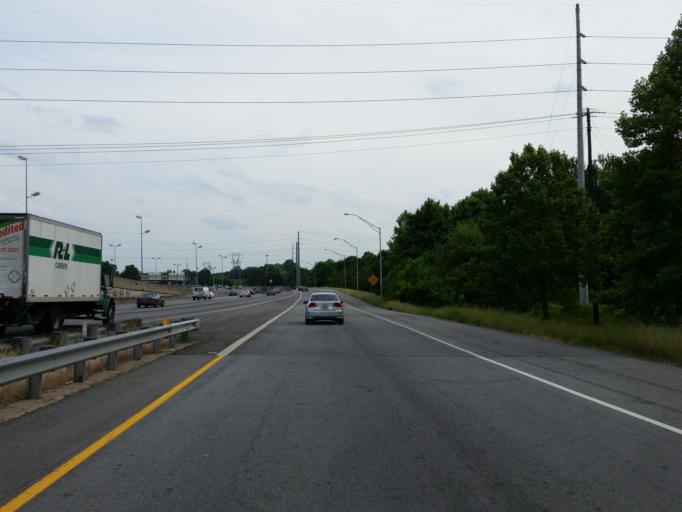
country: US
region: Georgia
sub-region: Fulton County
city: Hapeville
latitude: 33.6401
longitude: -84.4009
